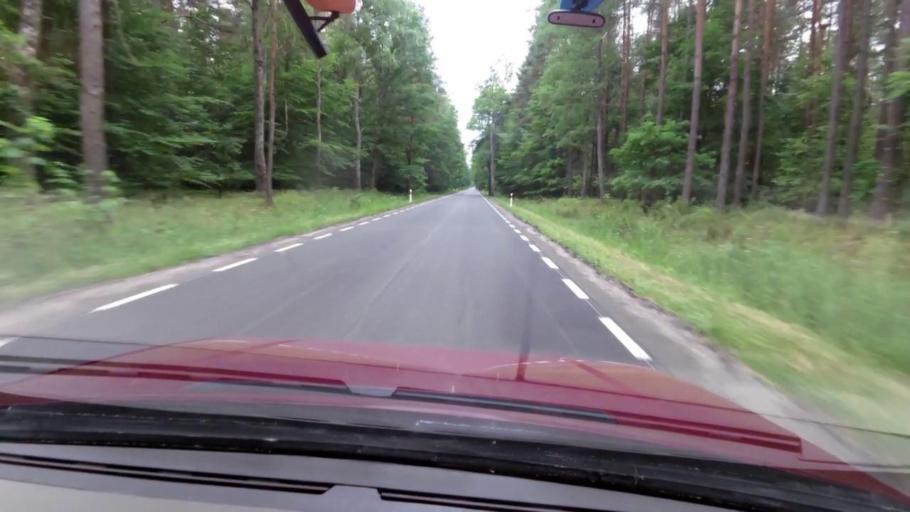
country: PL
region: Pomeranian Voivodeship
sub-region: Powiat slupski
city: Kepice
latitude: 54.2286
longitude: 16.8825
